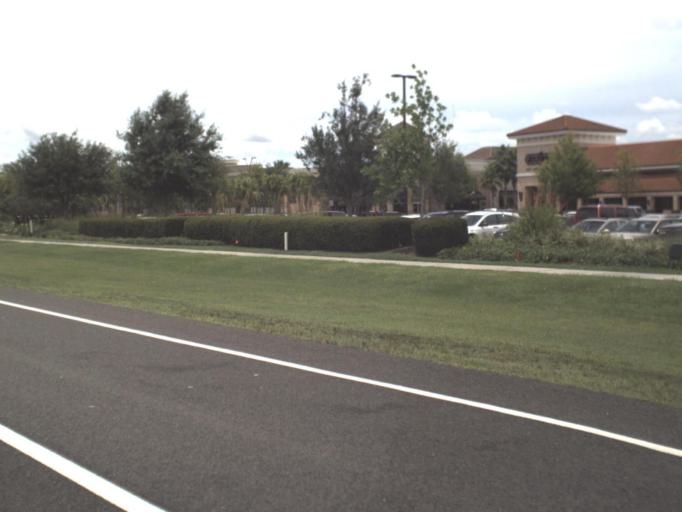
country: US
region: Florida
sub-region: Hillsborough County
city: Pebble Creek
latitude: 28.1872
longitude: -82.3475
